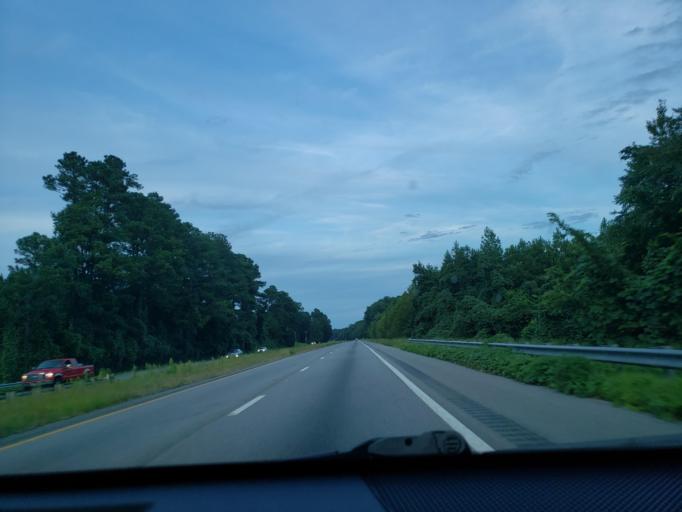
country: US
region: Virginia
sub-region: Southampton County
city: Courtland
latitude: 36.7021
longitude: -77.2502
